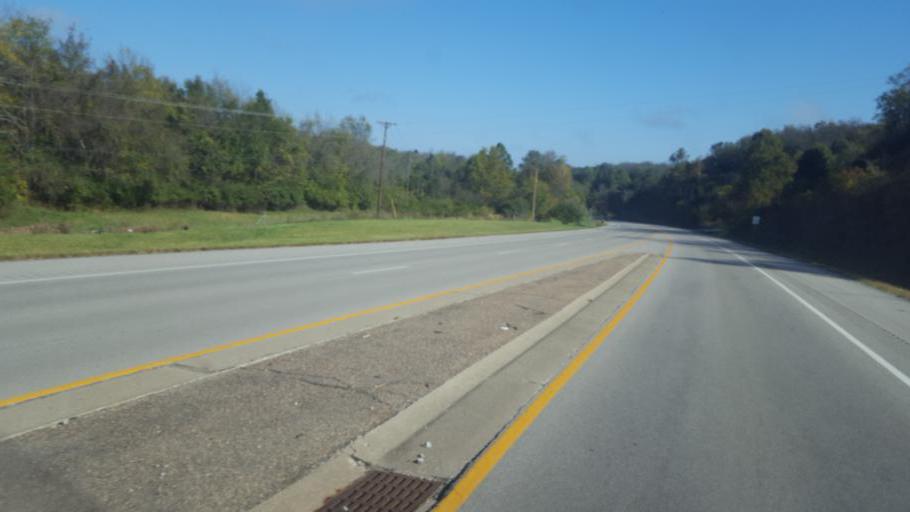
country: US
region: Kentucky
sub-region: Mason County
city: Maysville
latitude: 38.6056
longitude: -83.7592
